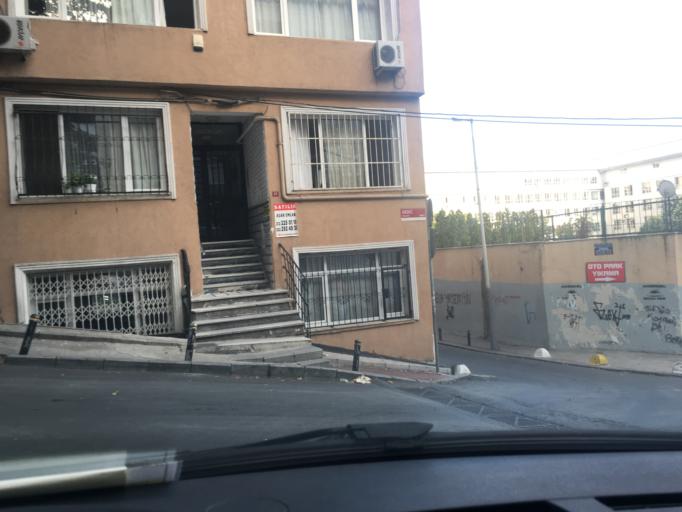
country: TR
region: Istanbul
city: Sisli
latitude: 41.0514
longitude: 28.9793
